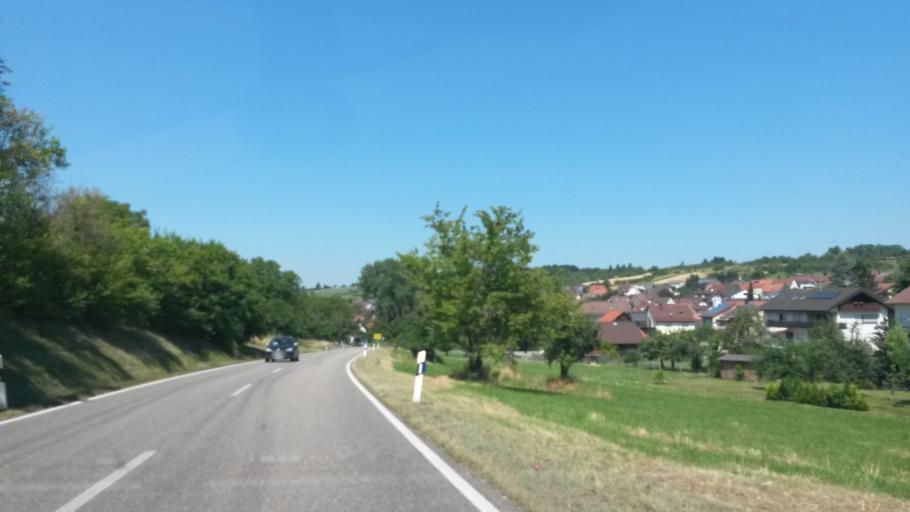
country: DE
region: Baden-Wuerttemberg
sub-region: Karlsruhe Region
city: Neuenburg
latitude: 48.8660
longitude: 8.5959
